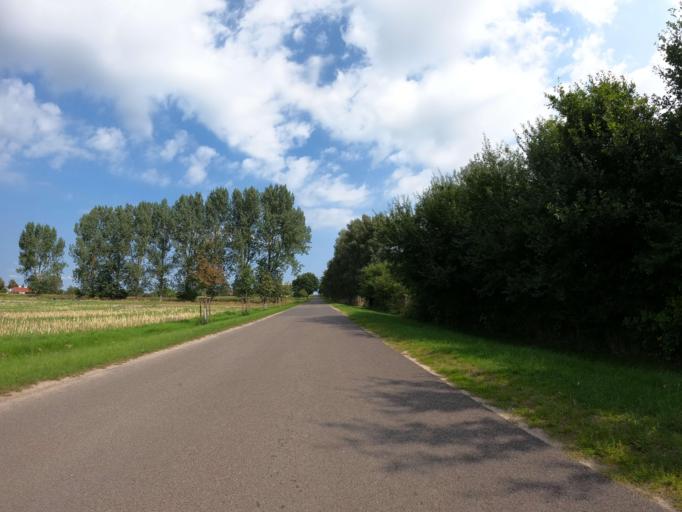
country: DE
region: Mecklenburg-Vorpommern
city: Malchow
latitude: 53.4575
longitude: 12.4780
